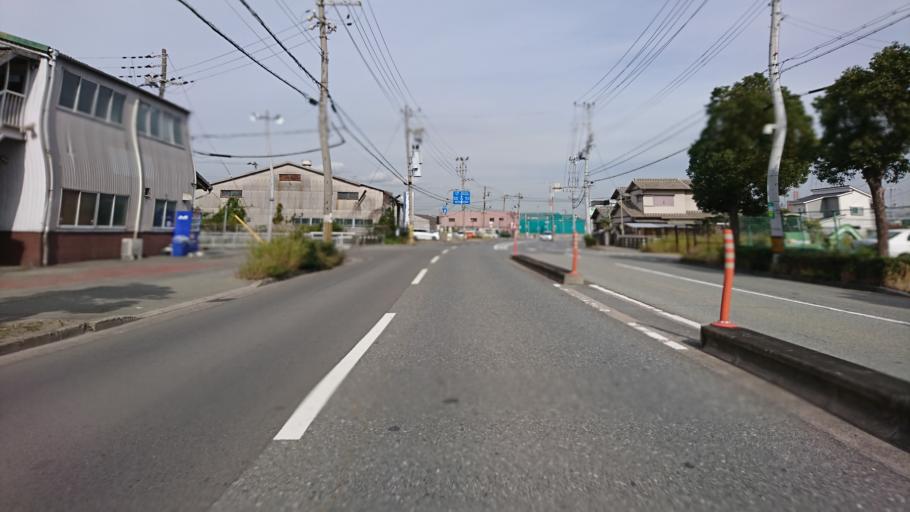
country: JP
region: Hyogo
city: Kakogawacho-honmachi
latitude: 34.7460
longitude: 134.8162
